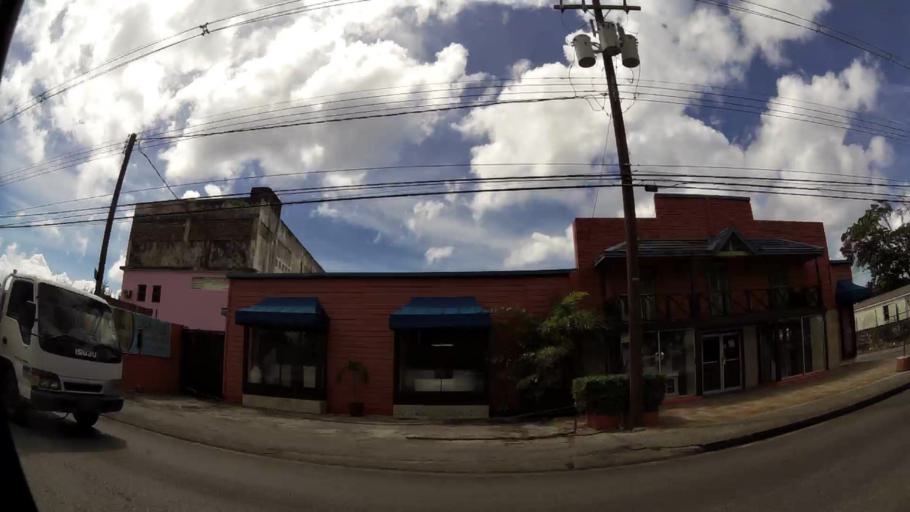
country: BB
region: Saint Michael
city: Bridgetown
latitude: 13.1006
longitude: -59.6229
